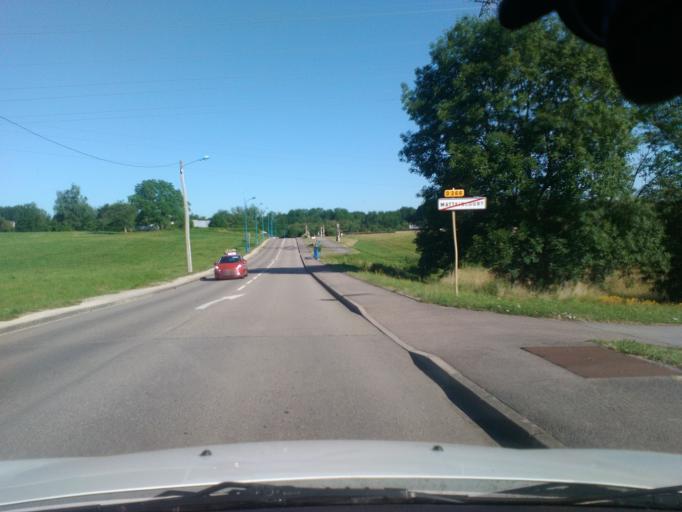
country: FR
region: Lorraine
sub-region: Departement des Vosges
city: Mirecourt
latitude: 48.2842
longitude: 6.1309
